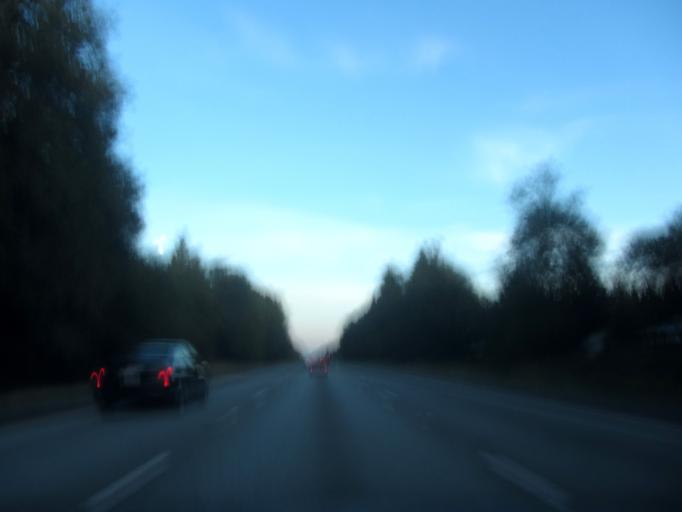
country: US
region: Washington
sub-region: Snohomish County
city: Bryant
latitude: 48.2573
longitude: -122.2598
